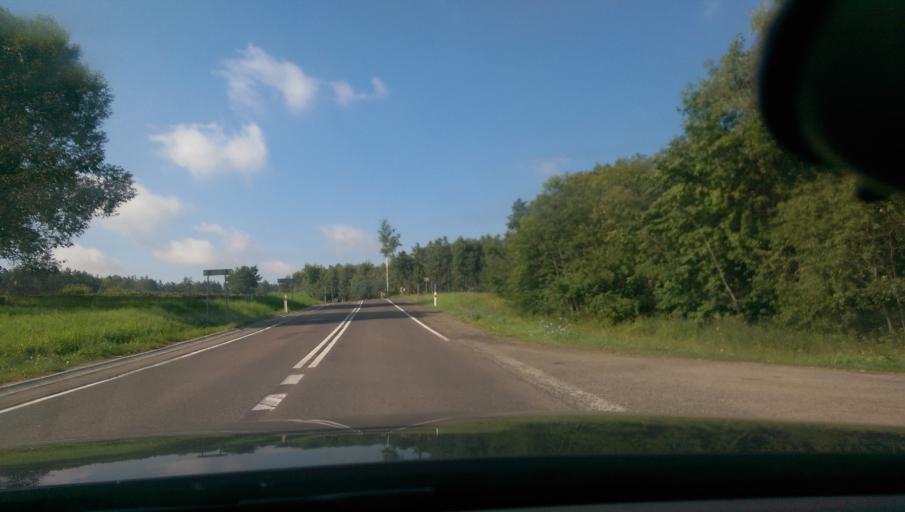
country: PL
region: Masovian Voivodeship
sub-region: Powiat plonski
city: Sochocin
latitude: 52.6787
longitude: 20.4589
